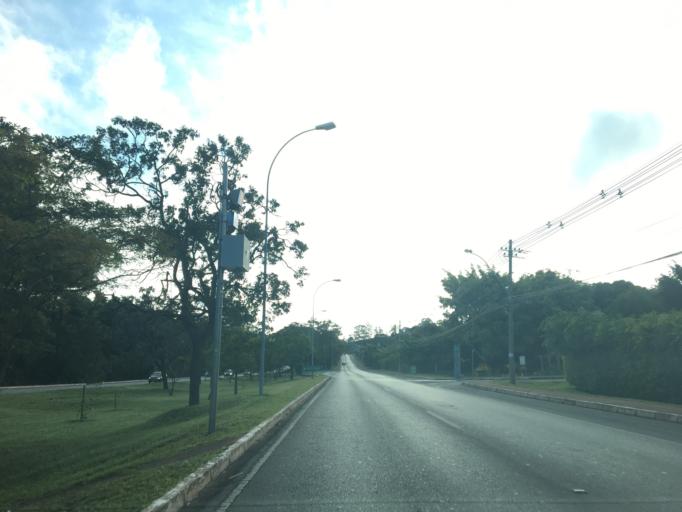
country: BR
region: Federal District
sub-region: Brasilia
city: Brasilia
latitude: -15.8288
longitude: -47.8101
